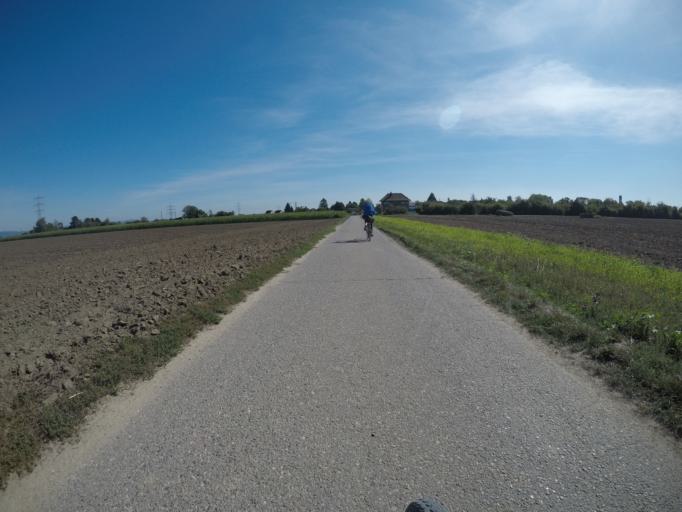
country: DE
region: Hesse
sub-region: Regierungsbezirk Darmstadt
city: Burstadt
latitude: 49.6635
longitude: 8.4118
